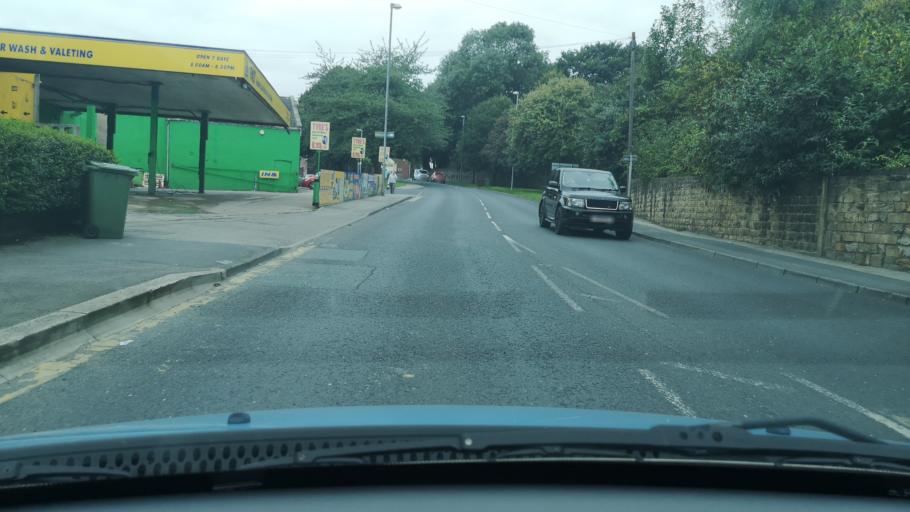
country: GB
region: England
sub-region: City and Borough of Wakefield
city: Pontefract
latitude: 53.6947
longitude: -1.3025
